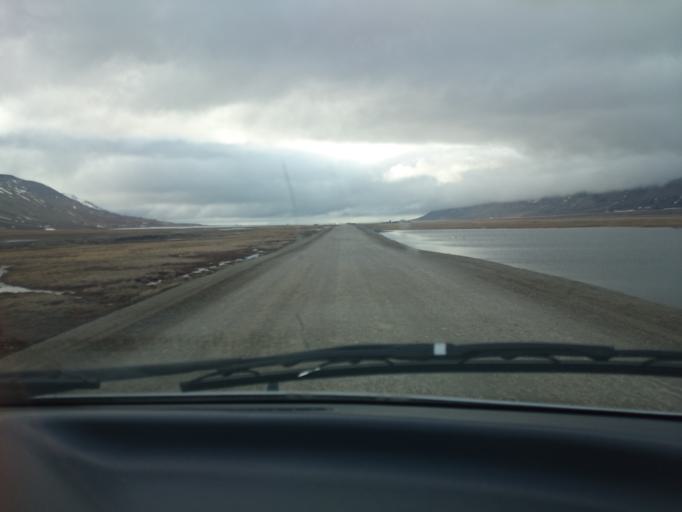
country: SJ
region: Svalbard
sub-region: Spitsbergen
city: Longyearbyen
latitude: 78.1950
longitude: 15.8526
